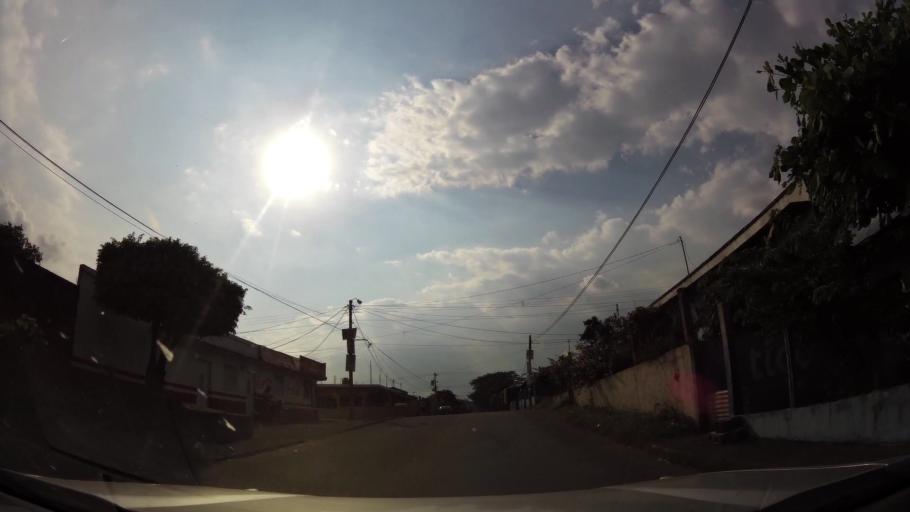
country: GT
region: Escuintla
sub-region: Municipio de Escuintla
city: Escuintla
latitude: 14.3159
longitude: -90.7951
